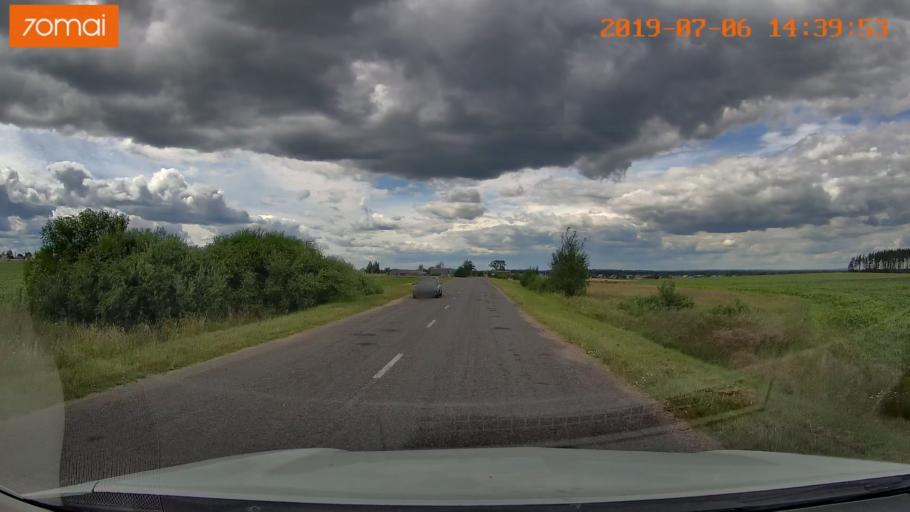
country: BY
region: Minsk
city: Ivyanyets
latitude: 53.9203
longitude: 26.6814
